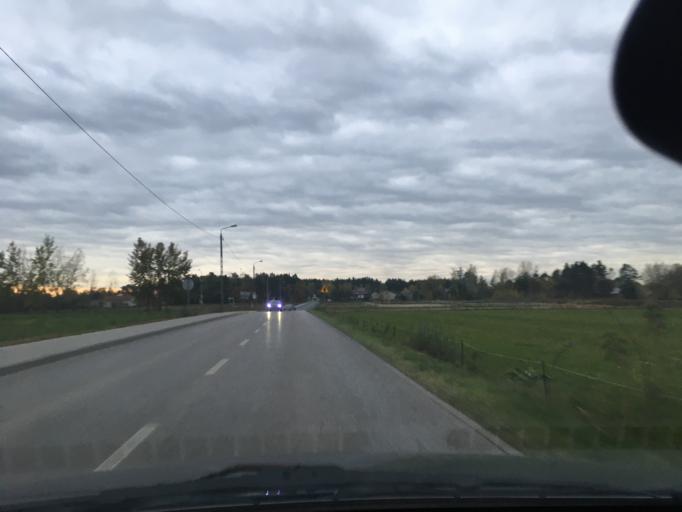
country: PL
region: Masovian Voivodeship
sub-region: Powiat piaseczynski
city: Lesznowola
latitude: 52.0713
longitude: 20.9351
